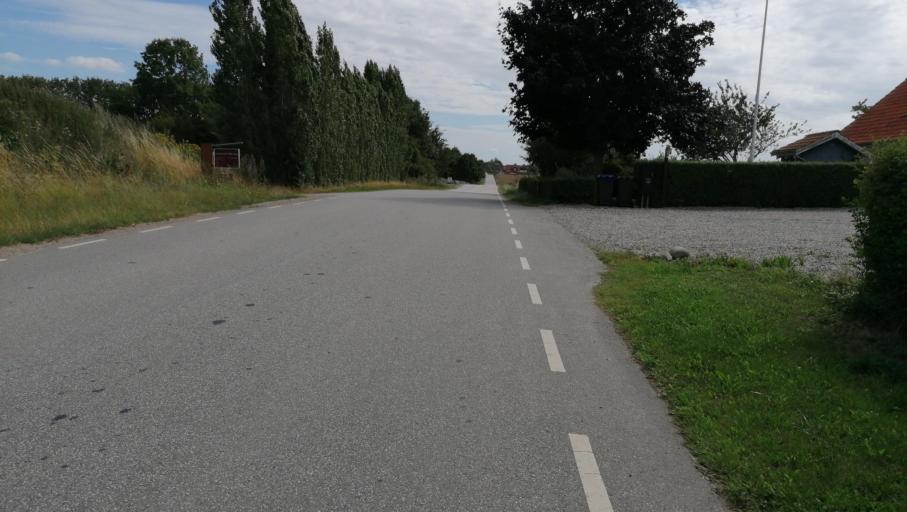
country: DK
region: Zealand
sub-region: Odsherred Kommune
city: Horve
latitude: 55.7591
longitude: 11.4397
